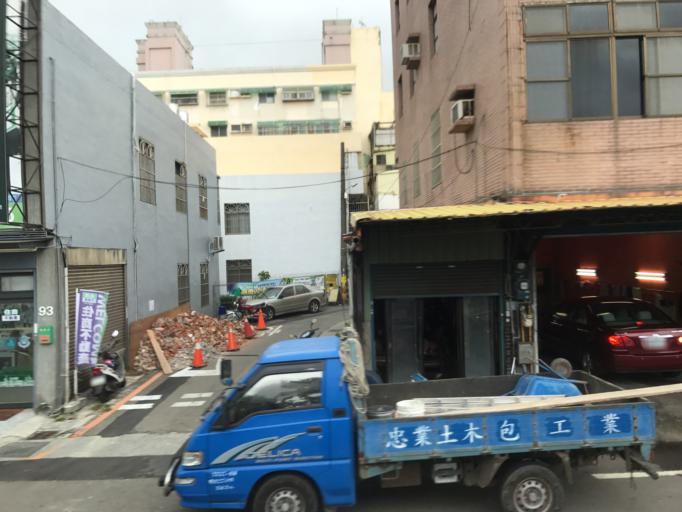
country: TW
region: Taiwan
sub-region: Hsinchu
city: Hsinchu
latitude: 24.8147
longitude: 120.9556
